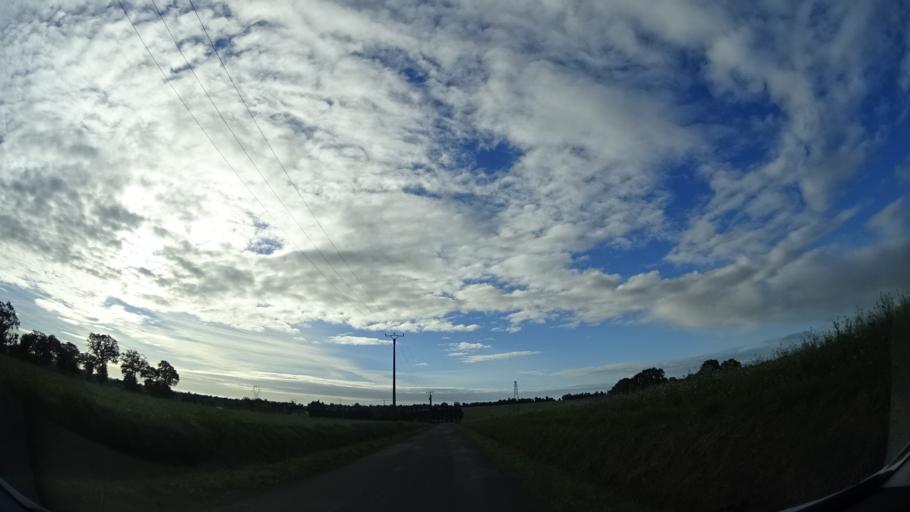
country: FR
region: Brittany
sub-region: Departement d'Ille-et-Vilaine
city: Geveze
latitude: 48.2049
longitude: -1.8067
